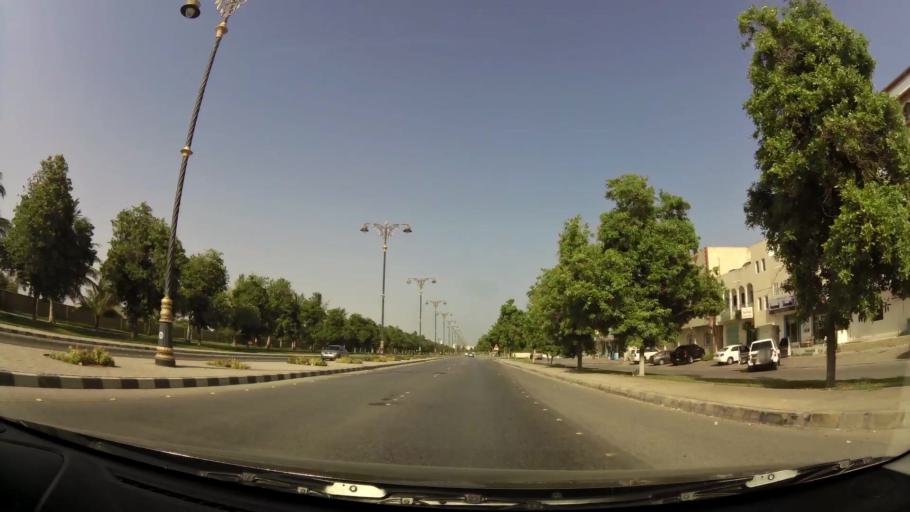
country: OM
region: Zufar
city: Salalah
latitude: 17.0044
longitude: 54.0514
